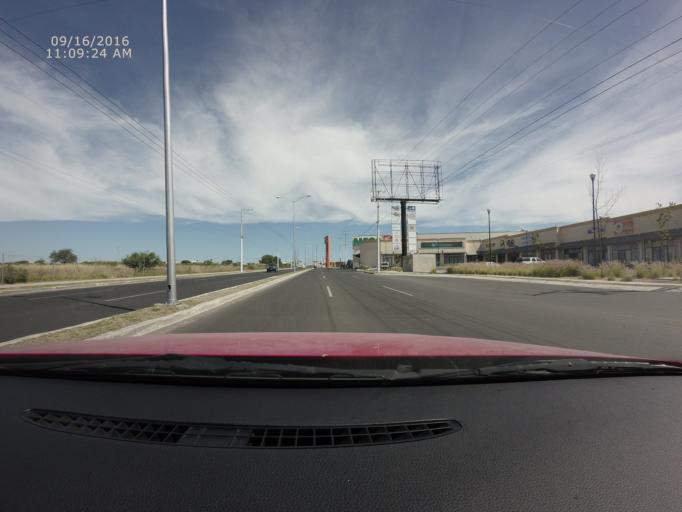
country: MX
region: Queretaro
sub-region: Queretaro
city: Sergio Villasenor
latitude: 20.6398
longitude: -100.4151
